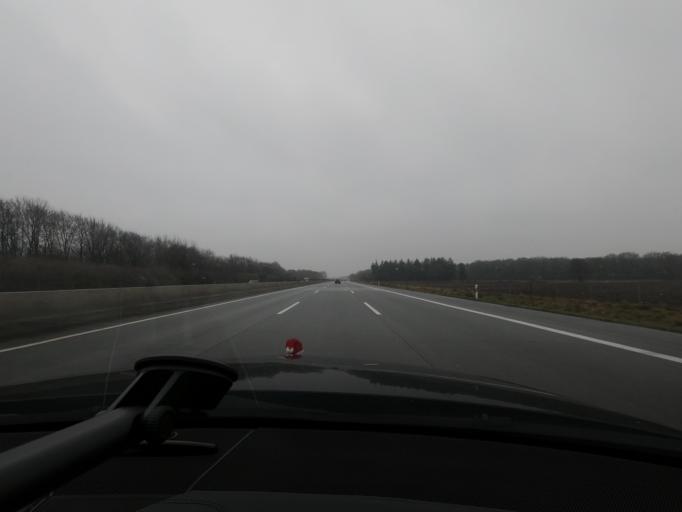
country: DE
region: Schleswig-Holstein
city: Padenstedt
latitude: 54.0276
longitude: 9.9323
